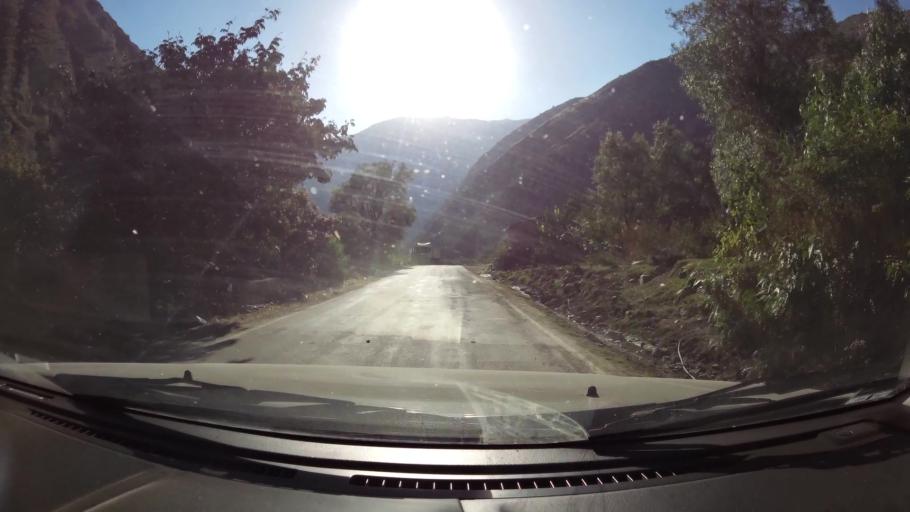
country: PE
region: Huancavelica
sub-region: Provincia de Churcampa
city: La Esmeralda
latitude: -12.5690
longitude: -74.6916
